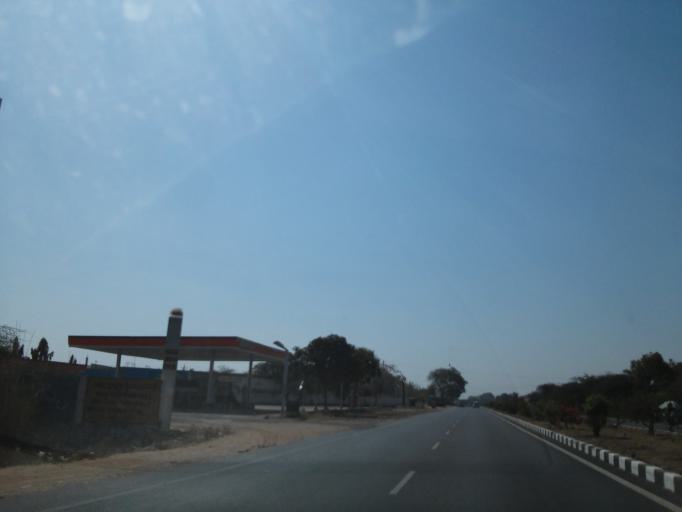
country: IN
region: Gujarat
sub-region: Sabar Kantha
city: Himatnagar
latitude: 23.5197
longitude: 72.9360
